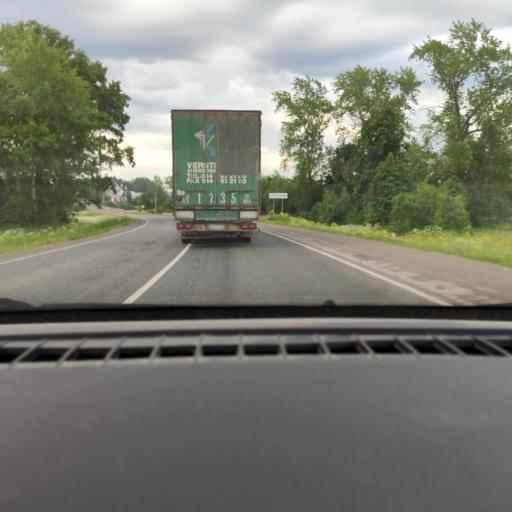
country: RU
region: Udmurtiya
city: Votkinsk
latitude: 57.3617
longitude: 54.4213
